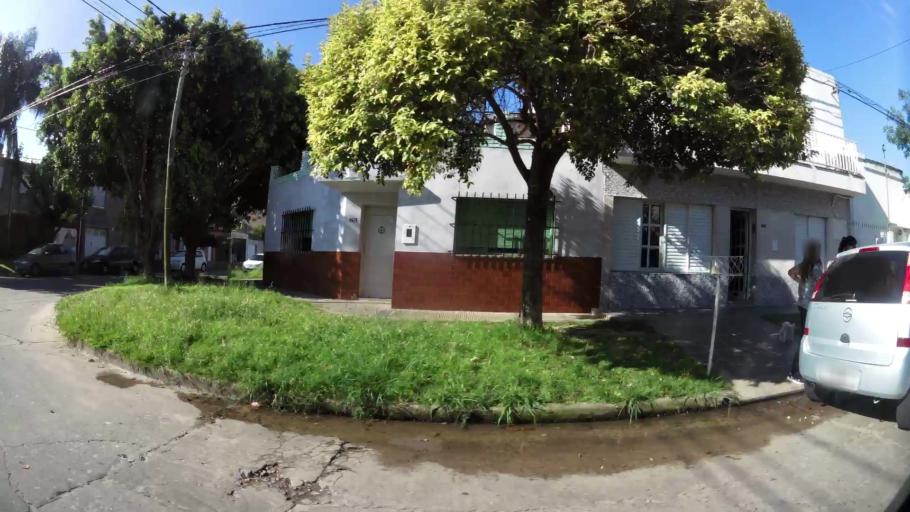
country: AR
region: Santa Fe
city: Santa Fe de la Vera Cruz
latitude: -31.6127
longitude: -60.6925
